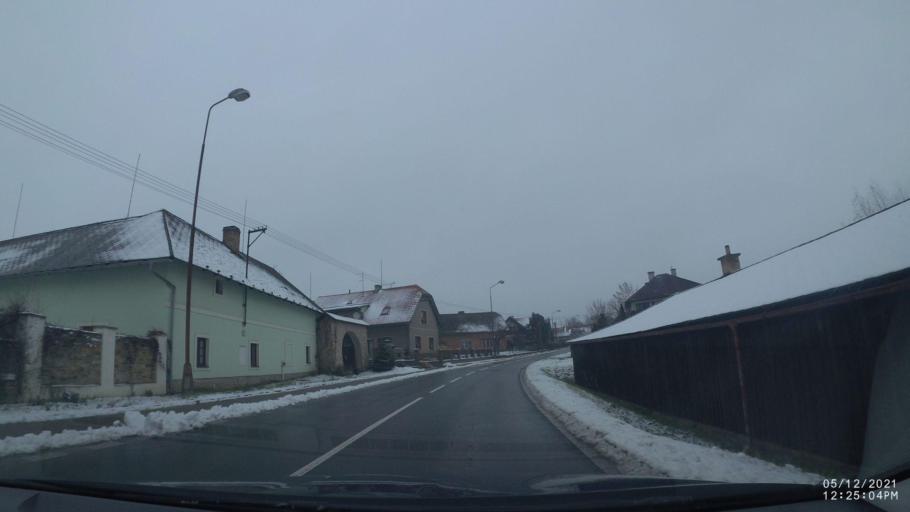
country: CZ
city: Ceske Mezirici
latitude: 50.3204
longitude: 16.0860
